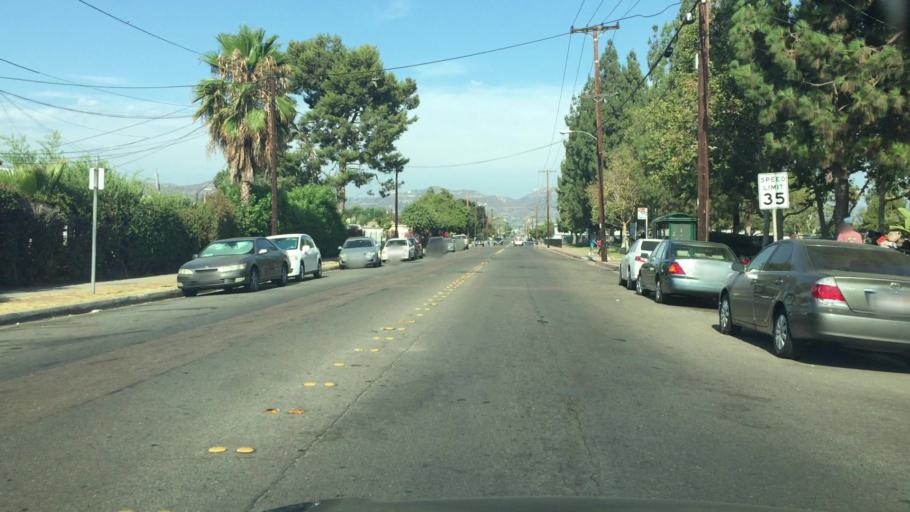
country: US
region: California
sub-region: San Diego County
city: Bostonia
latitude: 32.8002
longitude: -116.9440
